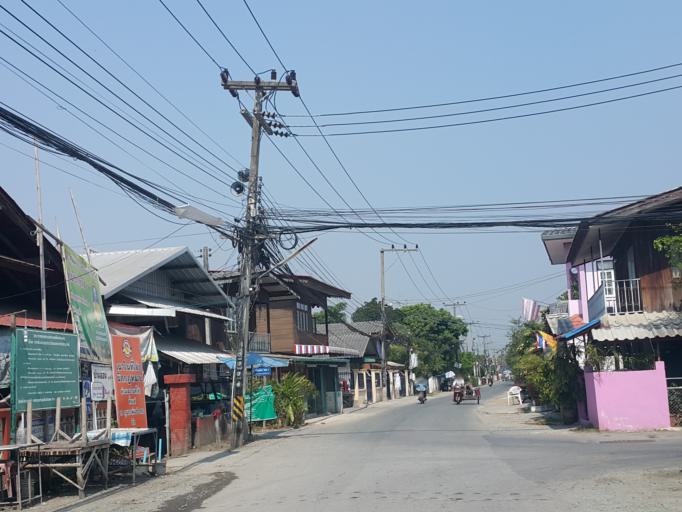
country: TH
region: Chiang Mai
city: San Kamphaeng
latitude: 18.7385
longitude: 99.1071
